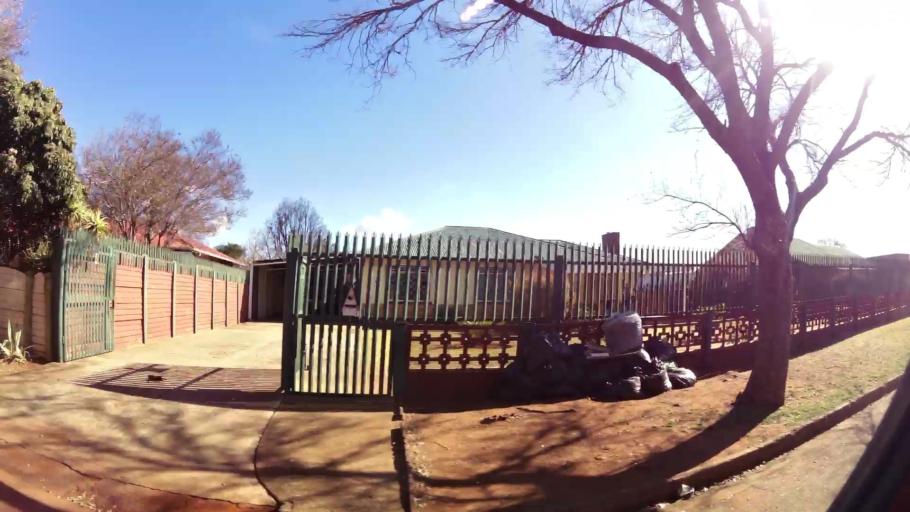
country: ZA
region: Gauteng
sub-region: West Rand District Municipality
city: Carletonville
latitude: -26.3632
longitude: 27.3942
